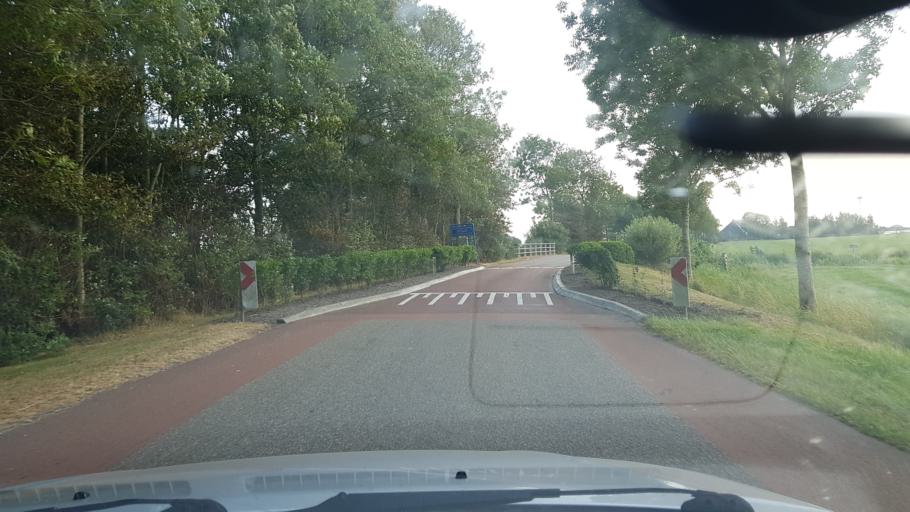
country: NL
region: Friesland
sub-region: Gemeente Ferwerderadiel
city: Burdaard
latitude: 53.3097
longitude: 5.8775
